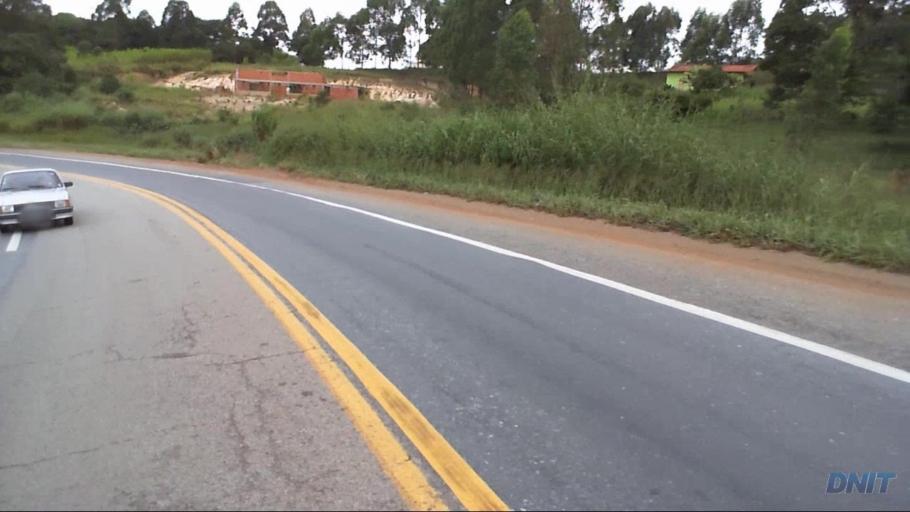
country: BR
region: Minas Gerais
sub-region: Caete
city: Caete
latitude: -19.7546
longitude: -43.5309
